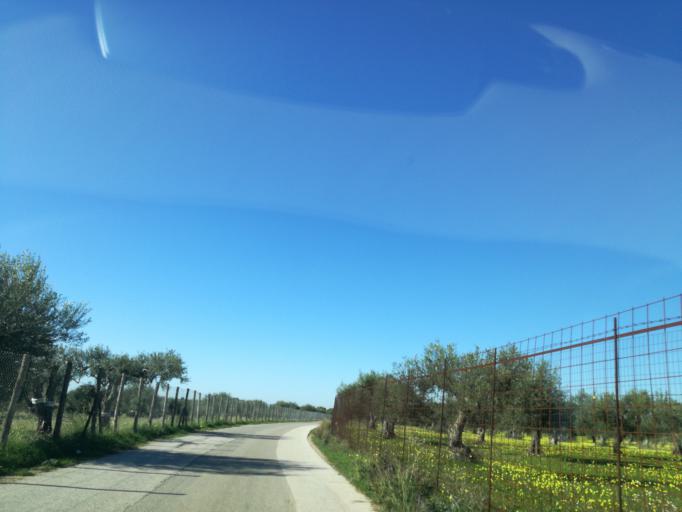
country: IT
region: Sicily
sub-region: Provincia di Caltanissetta
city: Niscemi
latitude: 37.0594
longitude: 14.3562
